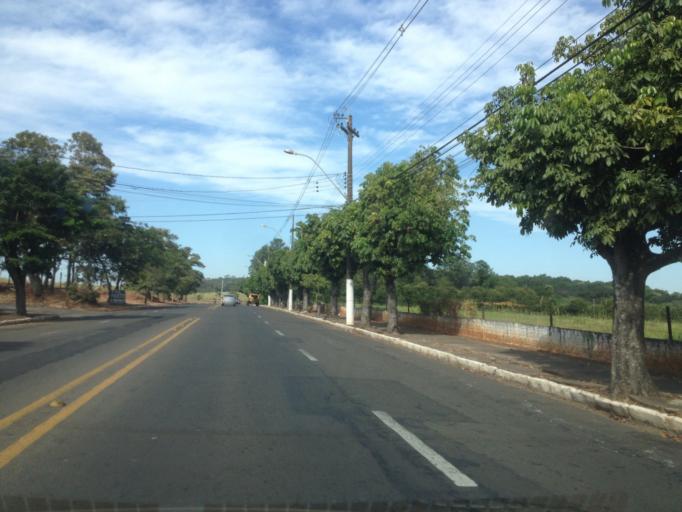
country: BR
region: Sao Paulo
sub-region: Marilia
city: Marilia
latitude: -22.1984
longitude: -49.9304
